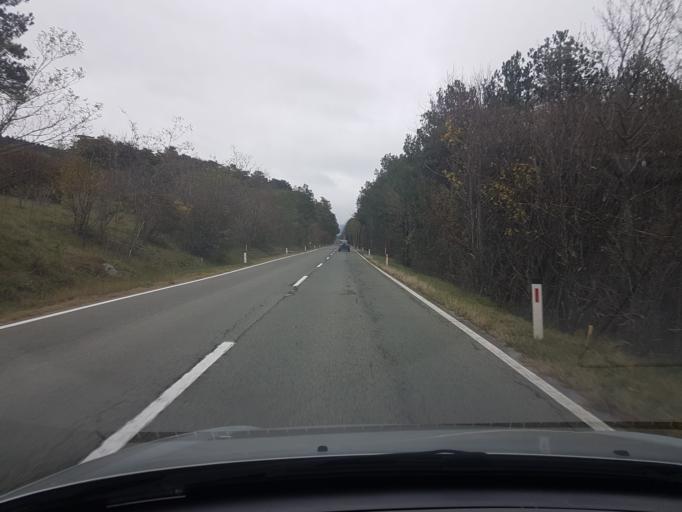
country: SI
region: Divaca
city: Divaca
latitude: 45.7305
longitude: 13.9629
